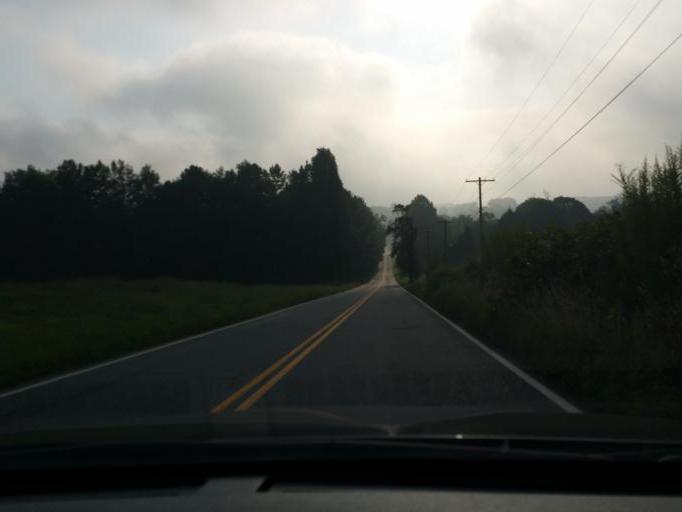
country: US
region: Maryland
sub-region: Cecil County
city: Rising Sun
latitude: 39.6716
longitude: -76.1083
